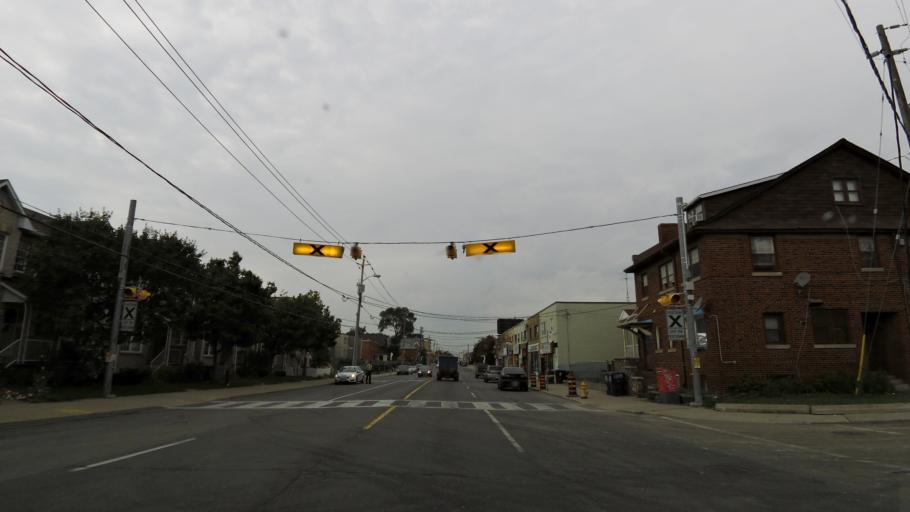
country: CA
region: Ontario
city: Toronto
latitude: 43.6878
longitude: -79.4919
